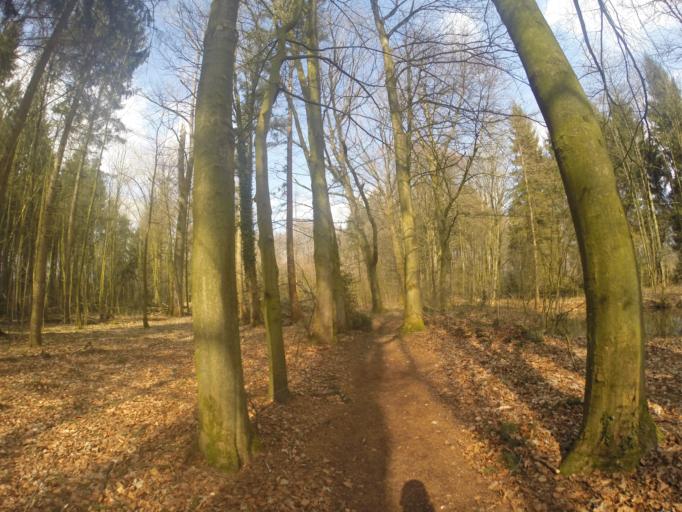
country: NL
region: Gelderland
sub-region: Gemeente Lochem
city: Almen
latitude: 52.1234
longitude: 6.3110
